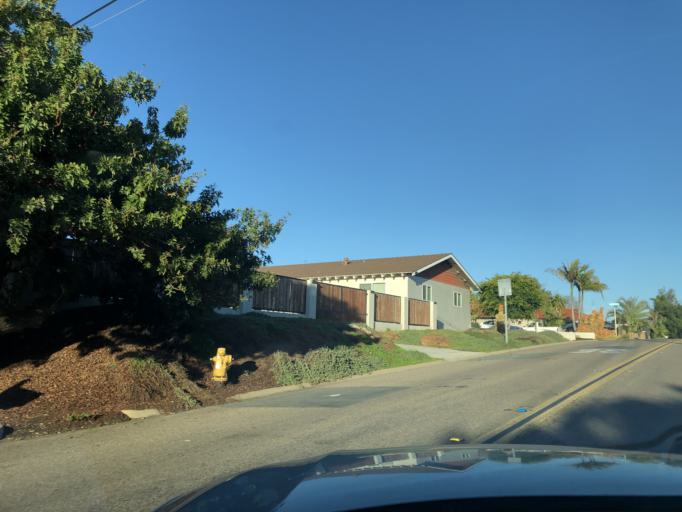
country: US
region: California
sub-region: San Diego County
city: Chula Vista
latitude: 32.6538
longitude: -117.0622
